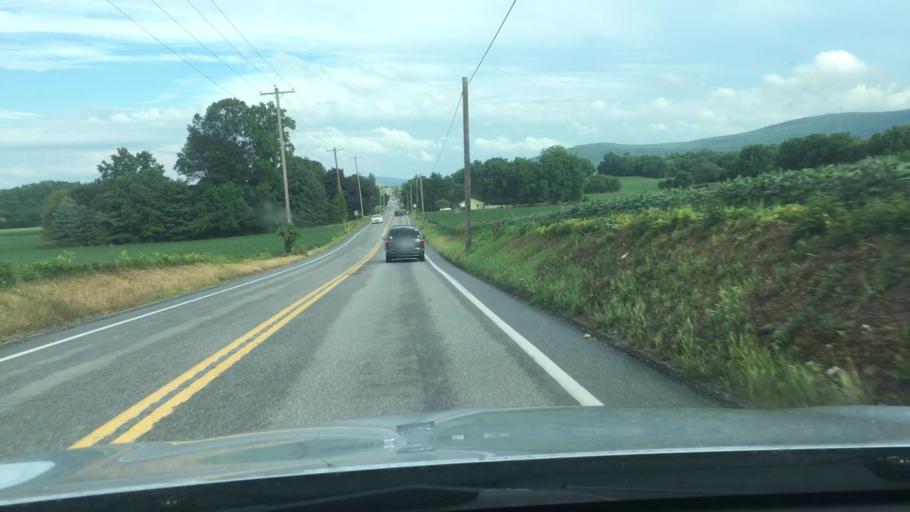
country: US
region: Pennsylvania
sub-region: Cumberland County
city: Boiling Springs
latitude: 40.1651
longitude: -77.1044
